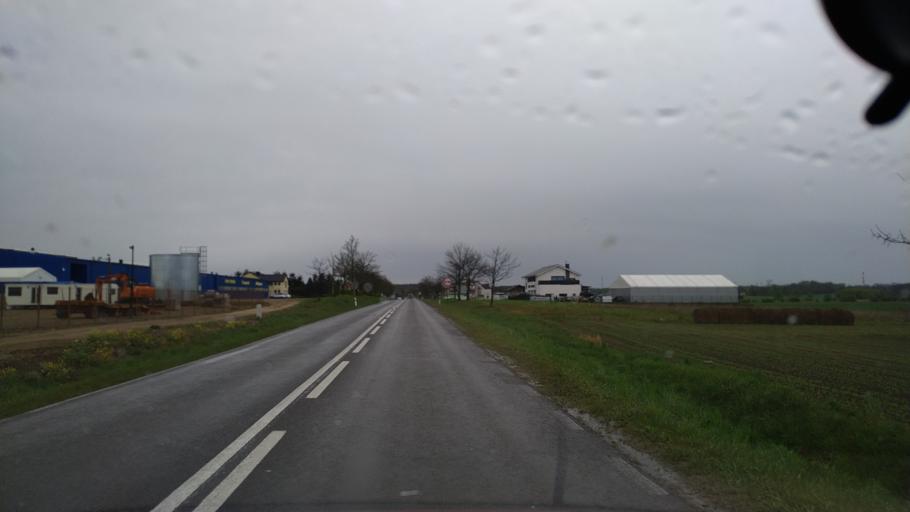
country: PL
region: Greater Poland Voivodeship
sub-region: Powiat zlotowski
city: Zlotow
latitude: 53.3409
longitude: 17.0151
